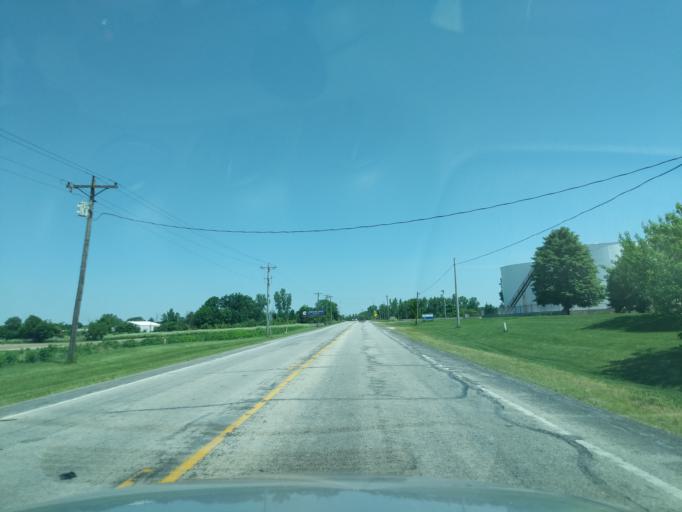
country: US
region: Indiana
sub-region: Whitley County
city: Columbia City
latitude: 41.0836
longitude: -85.4701
